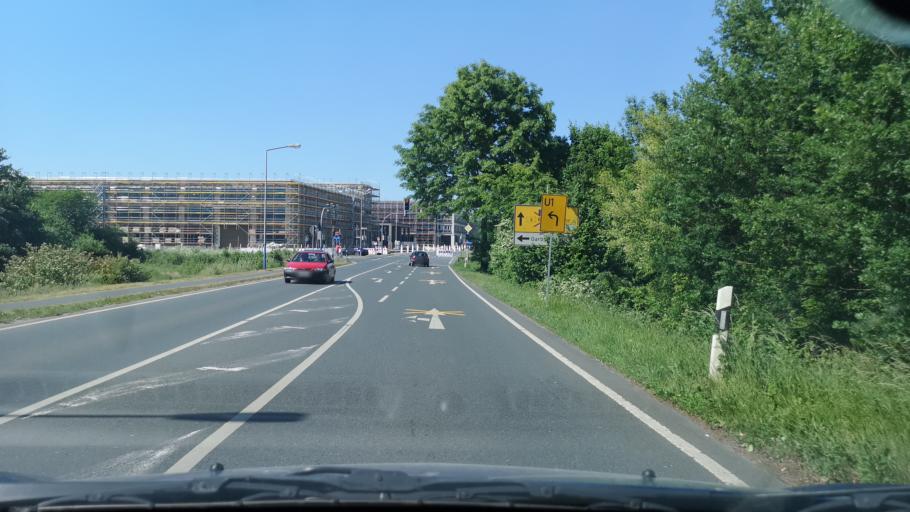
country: DE
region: Lower Saxony
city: Garbsen-Mitte
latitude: 52.4234
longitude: 9.6176
